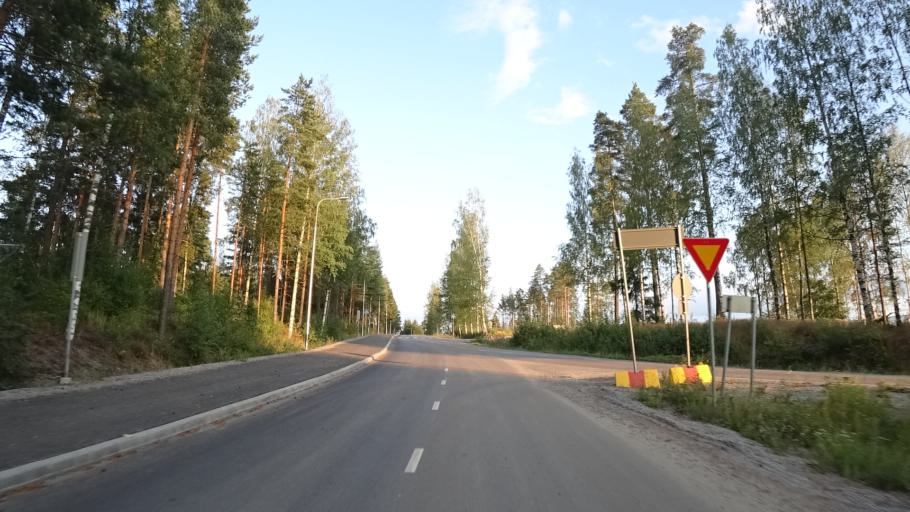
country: FI
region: Southern Savonia
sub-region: Savonlinna
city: Punkaharju
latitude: 61.7587
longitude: 29.3844
